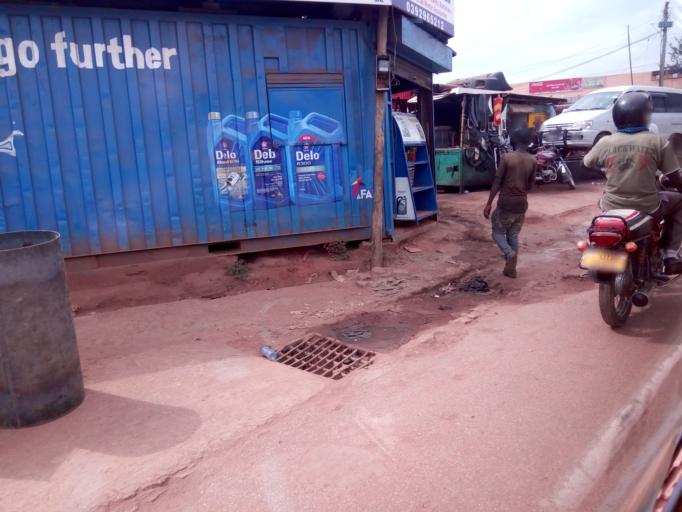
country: UG
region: Central Region
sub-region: Kampala District
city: Kampala
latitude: 0.3087
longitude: 32.5694
